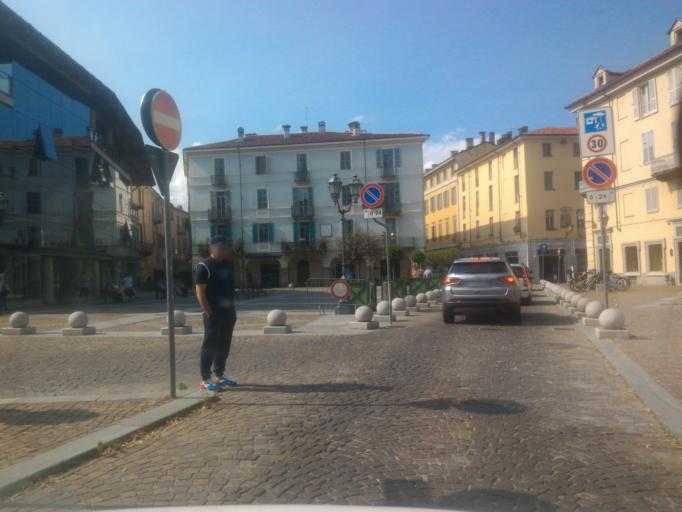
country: IT
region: Piedmont
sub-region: Provincia di Torino
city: Pinerolo
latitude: 44.8852
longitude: 7.3323
